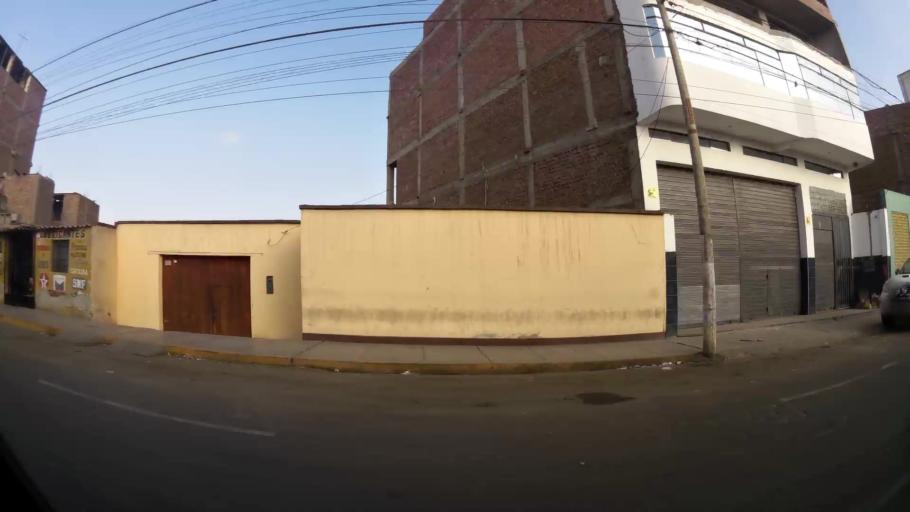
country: PE
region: La Libertad
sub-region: Provincia de Trujillo
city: El Porvenir
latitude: -8.0984
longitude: -79.0130
